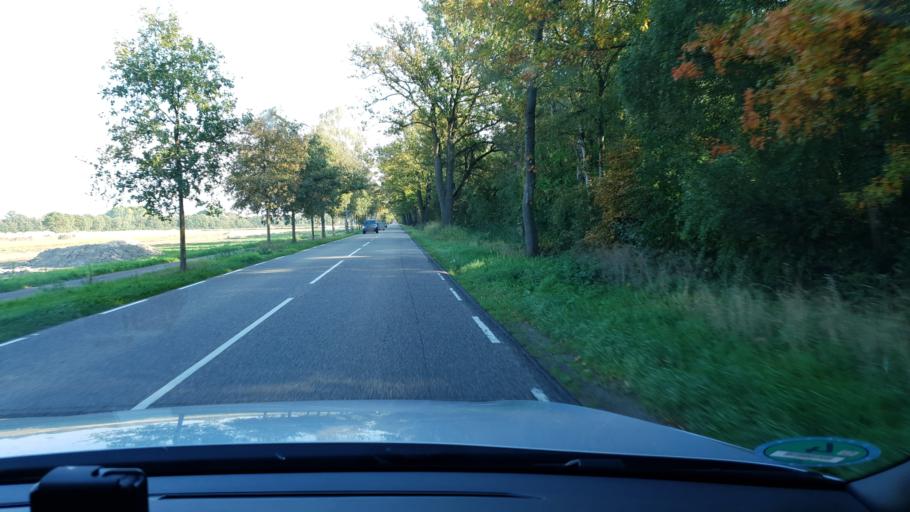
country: NL
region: North Brabant
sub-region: Gemeente Best
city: Best
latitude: 51.4760
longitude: 5.3788
